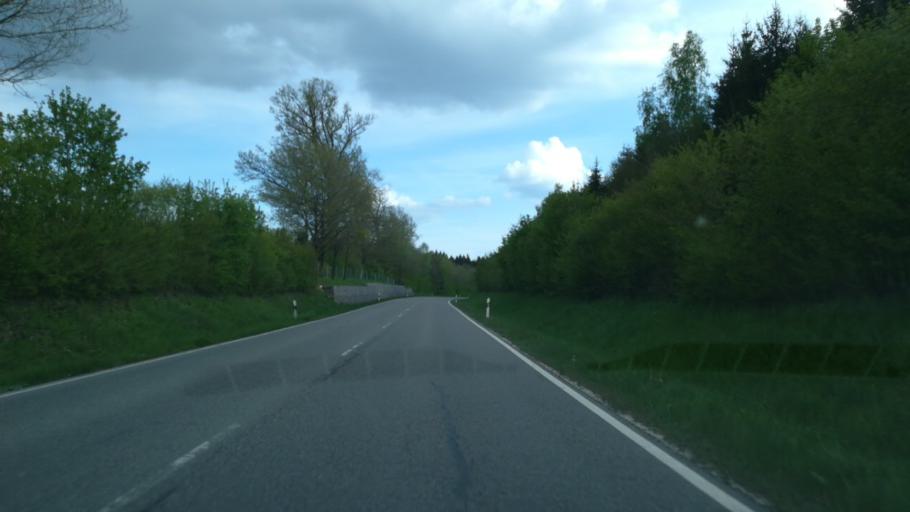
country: DE
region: Baden-Wuerttemberg
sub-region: Tuebingen Region
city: Messkirch
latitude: 47.9819
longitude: 9.0799
